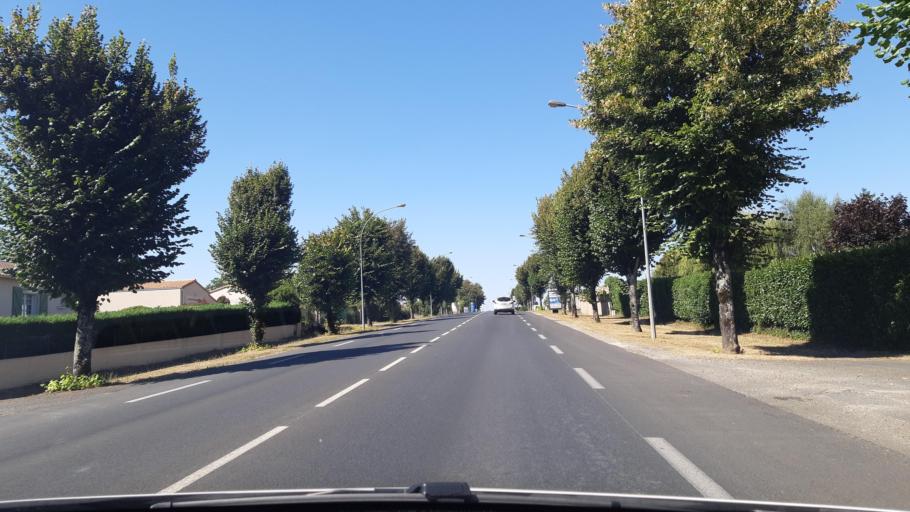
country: FR
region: Poitou-Charentes
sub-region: Departement des Deux-Sevres
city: Saivres
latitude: 46.4091
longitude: -0.2186
